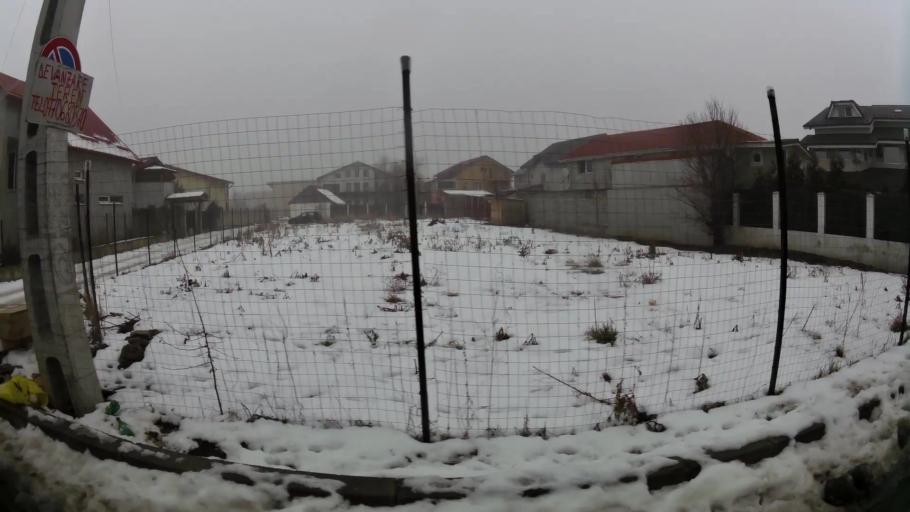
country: RO
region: Ilfov
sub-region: Comuna Chiajna
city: Chiajna
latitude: 44.4543
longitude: 25.9861
